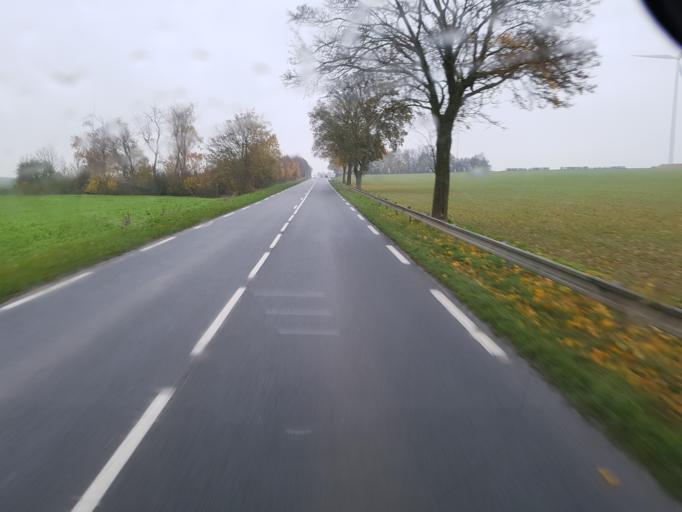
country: FR
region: Picardie
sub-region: Departement de l'Aisne
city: Omissy
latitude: 49.8958
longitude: 3.2634
